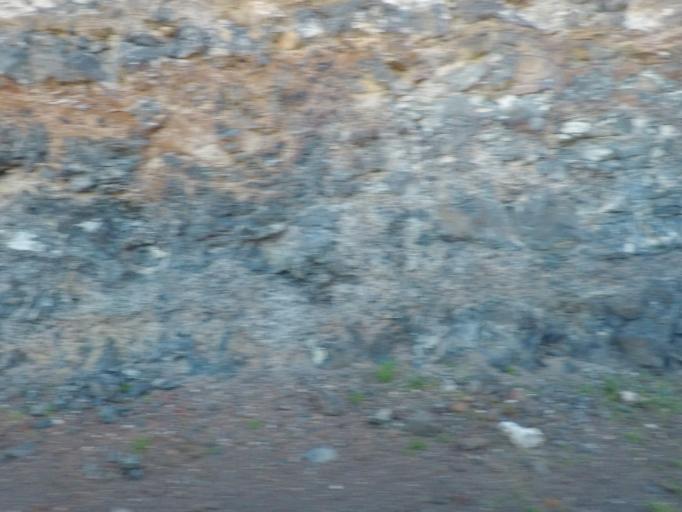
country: ES
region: Canary Islands
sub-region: Provincia de Santa Cruz de Tenerife
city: San Sebastian de la Gomera
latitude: 28.0852
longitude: -17.1243
